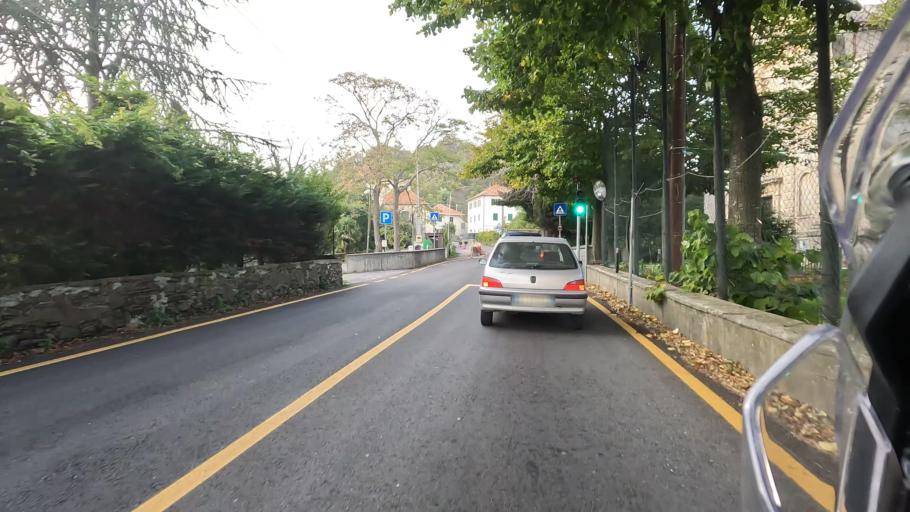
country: IT
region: Liguria
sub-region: Provincia di Savona
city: Osteria dei Cacciatori-Stella
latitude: 44.4179
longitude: 8.4803
